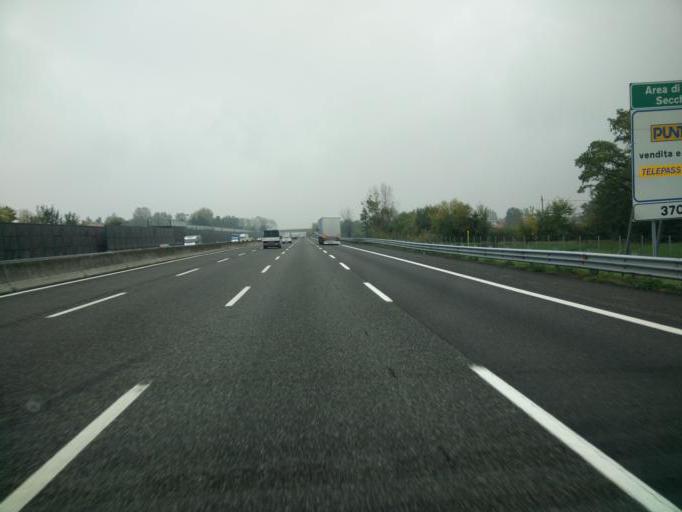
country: IT
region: Emilia-Romagna
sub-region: Provincia di Modena
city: Baggiovara
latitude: 44.6323
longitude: 10.8764
